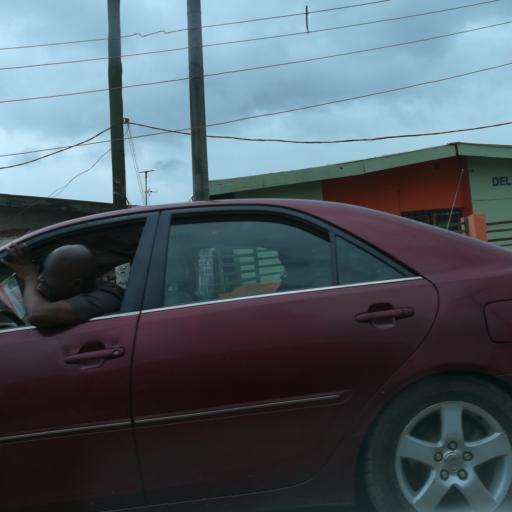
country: NG
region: Lagos
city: Agege
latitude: 6.6083
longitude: 3.2958
